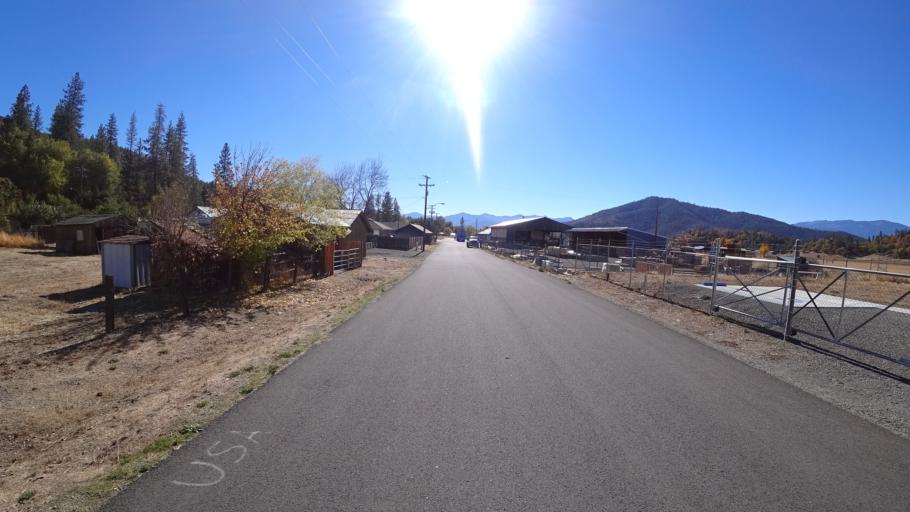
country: US
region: California
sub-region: Siskiyou County
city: Yreka
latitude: 41.6142
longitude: -122.8383
